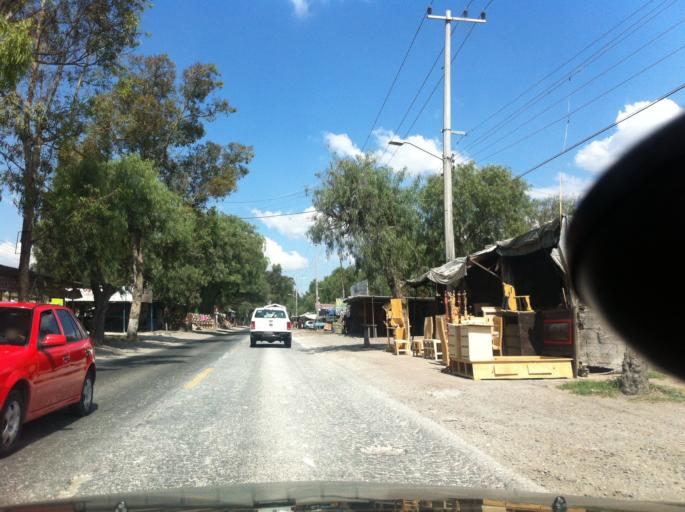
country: MX
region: Mexico
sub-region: Cuautitlan
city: La Providencia
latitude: 19.7678
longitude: -99.1232
